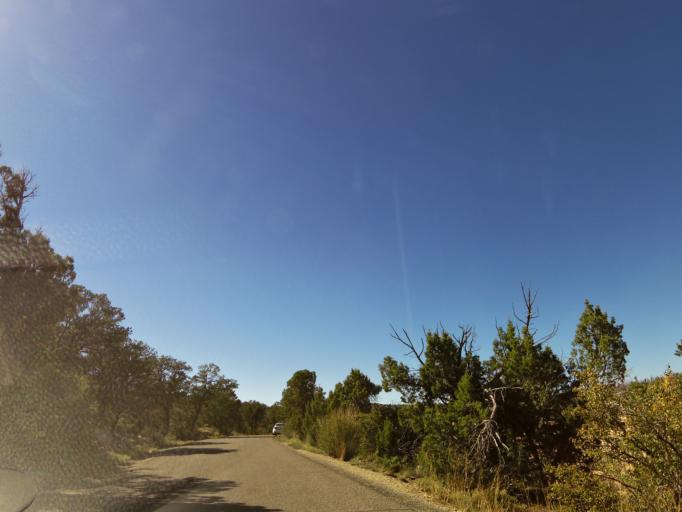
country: US
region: Colorado
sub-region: Montezuma County
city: Cortez
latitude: 37.1636
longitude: -108.4775
